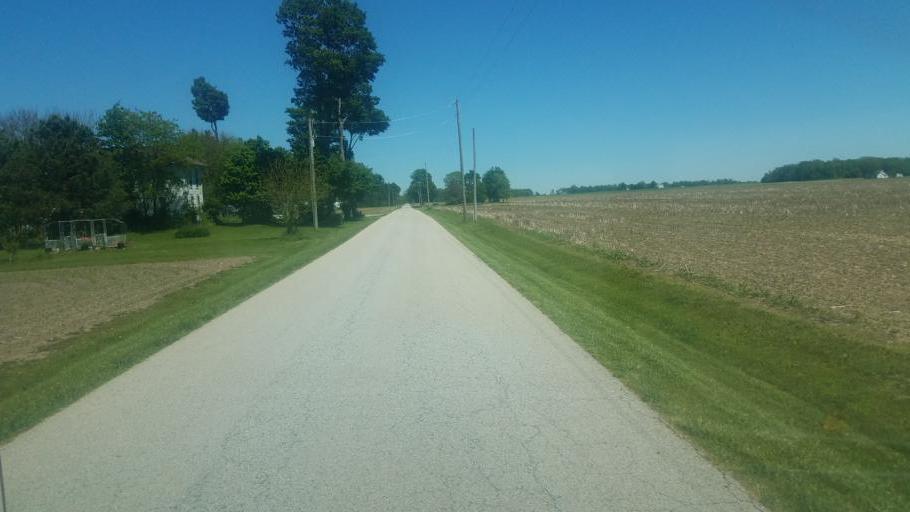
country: US
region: Ohio
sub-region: Champaign County
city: Saint Paris
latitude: 40.1997
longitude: -84.0497
